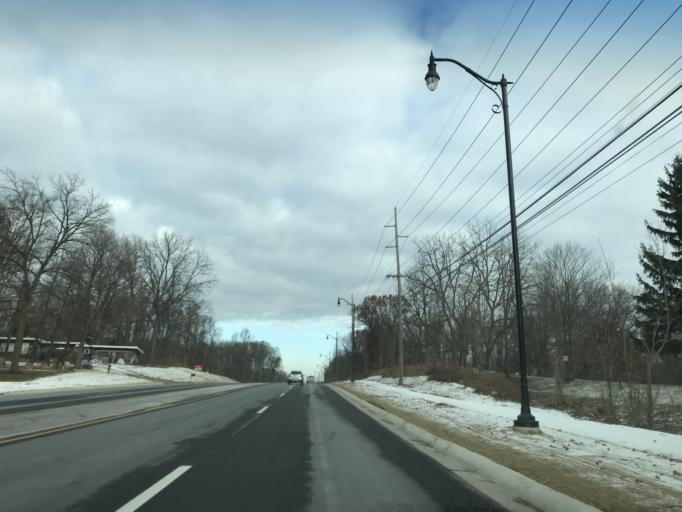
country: US
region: Michigan
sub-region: Oakland County
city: Clarkston
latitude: 42.7430
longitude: -83.3799
